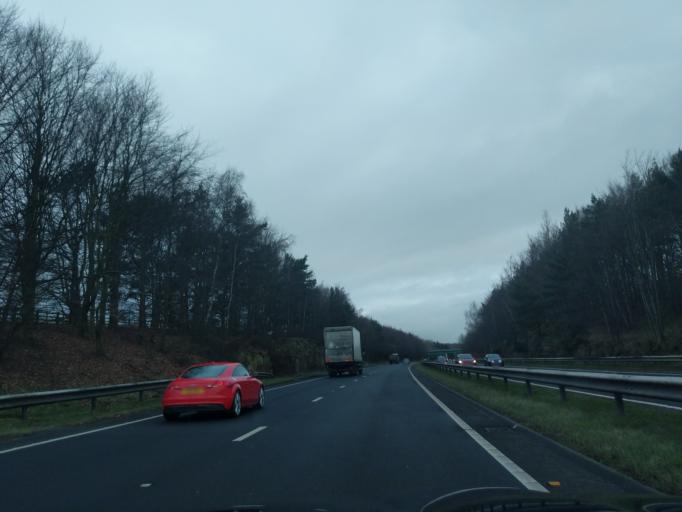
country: GB
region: England
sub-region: Northumberland
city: Stannington
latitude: 55.0900
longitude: -1.6551
